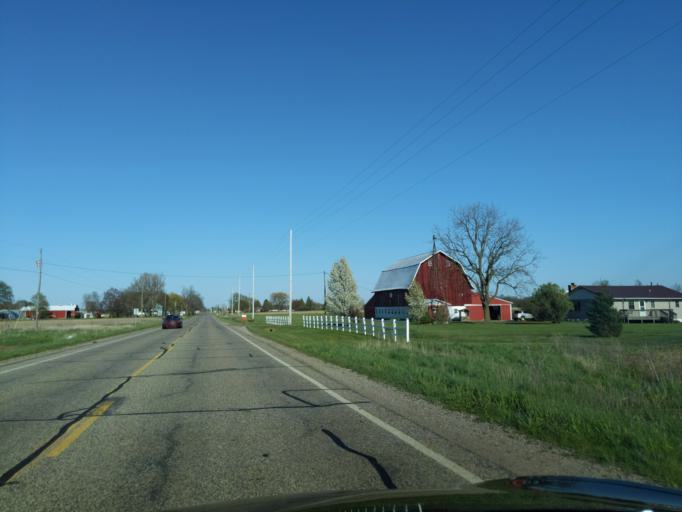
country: US
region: Michigan
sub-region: Ionia County
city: Ionia
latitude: 42.8859
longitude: -85.0403
